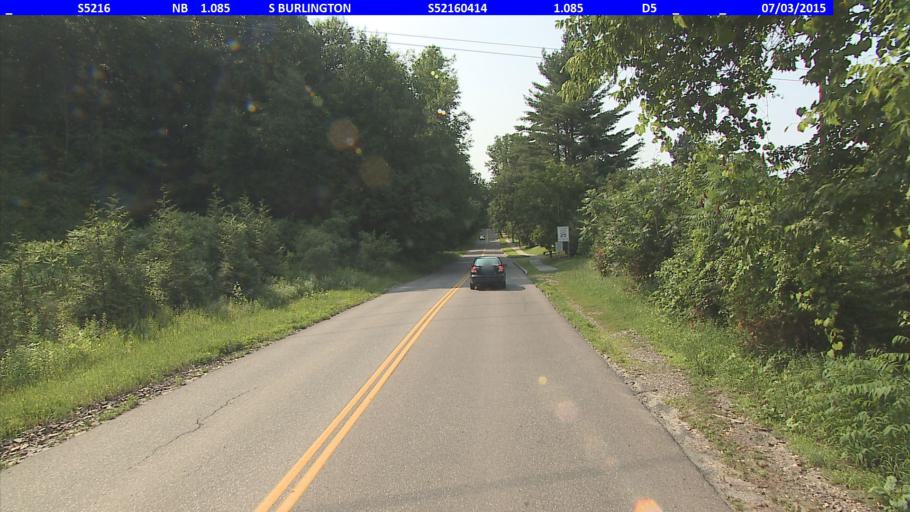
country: US
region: Vermont
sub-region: Chittenden County
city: Winooski
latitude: 44.4806
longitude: -73.1797
